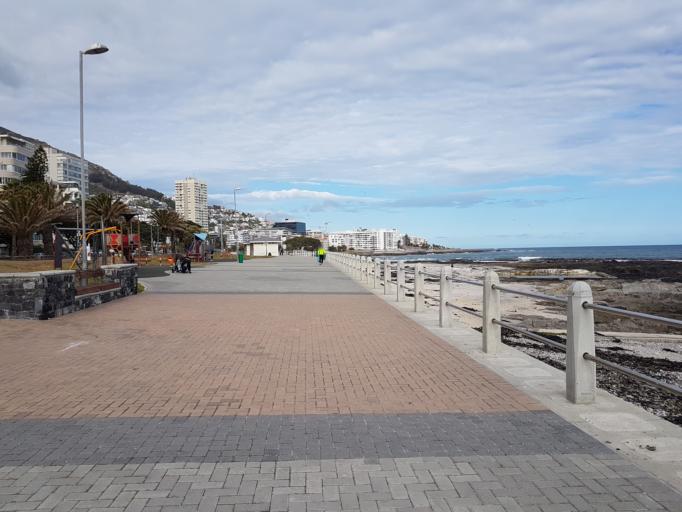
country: ZA
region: Western Cape
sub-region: City of Cape Town
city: Cape Town
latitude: -33.9138
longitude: 18.3873
